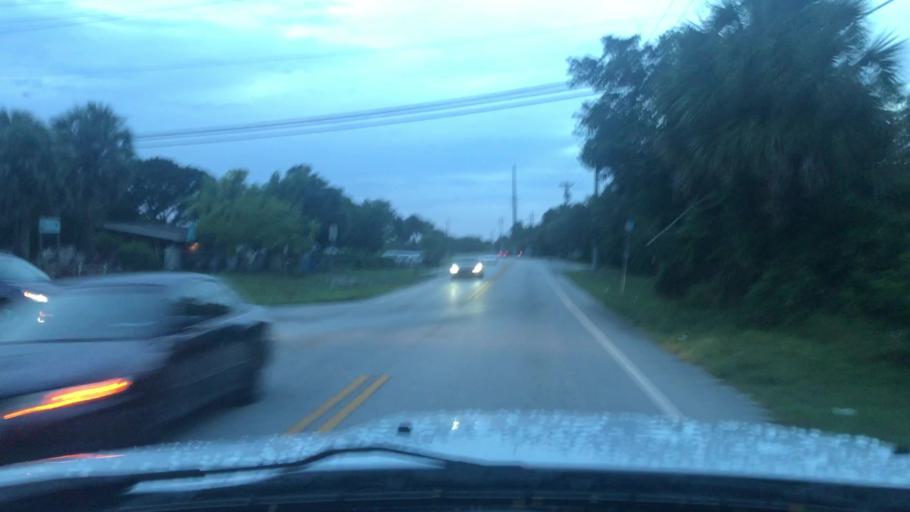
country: US
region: Florida
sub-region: Indian River County
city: Florida Ridge
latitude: 27.6014
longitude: -80.3858
